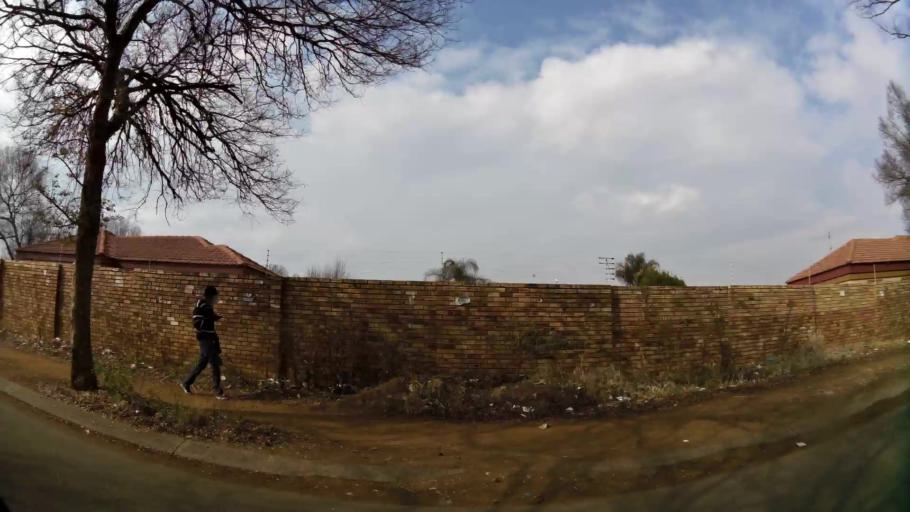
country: ZA
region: Gauteng
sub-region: Sedibeng District Municipality
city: Vanderbijlpark
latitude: -26.6906
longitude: 27.8399
